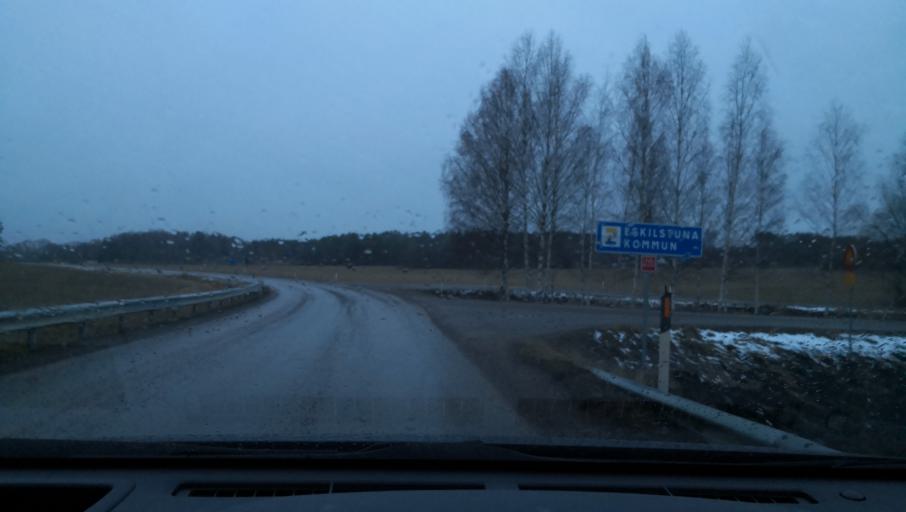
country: SE
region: Soedermanland
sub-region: Eskilstuna Kommun
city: Arla
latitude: 59.4514
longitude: 16.7263
